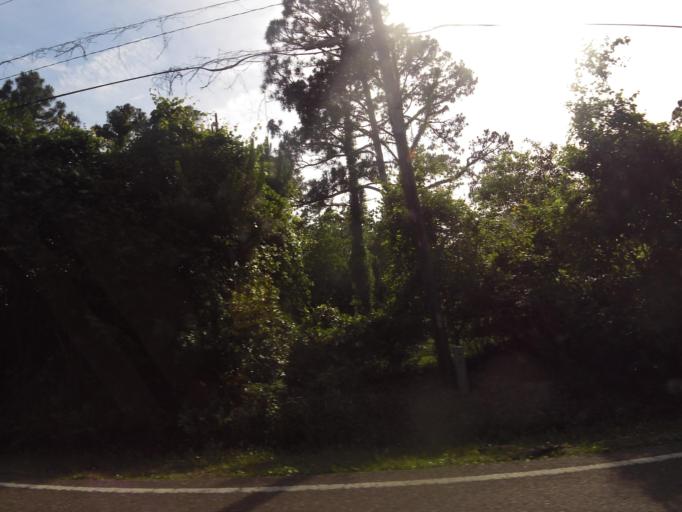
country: US
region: Florida
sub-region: Nassau County
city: Fernandina Beach
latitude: 30.5250
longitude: -81.4825
